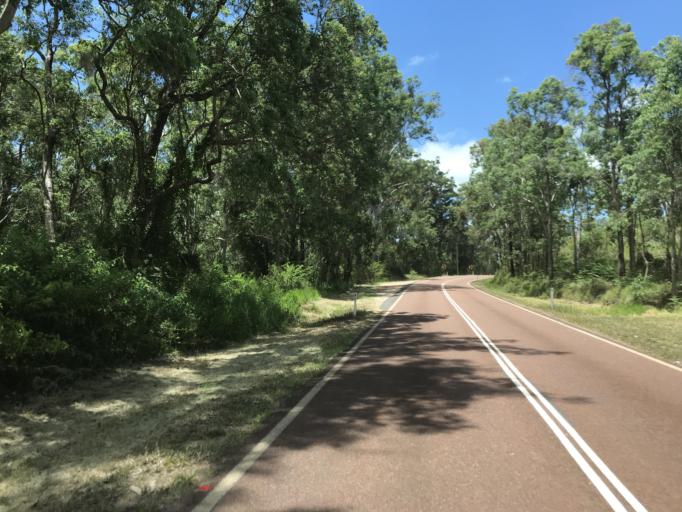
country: AU
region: Queensland
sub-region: Tablelands
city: Ravenshoe
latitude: -17.6008
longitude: 145.4778
